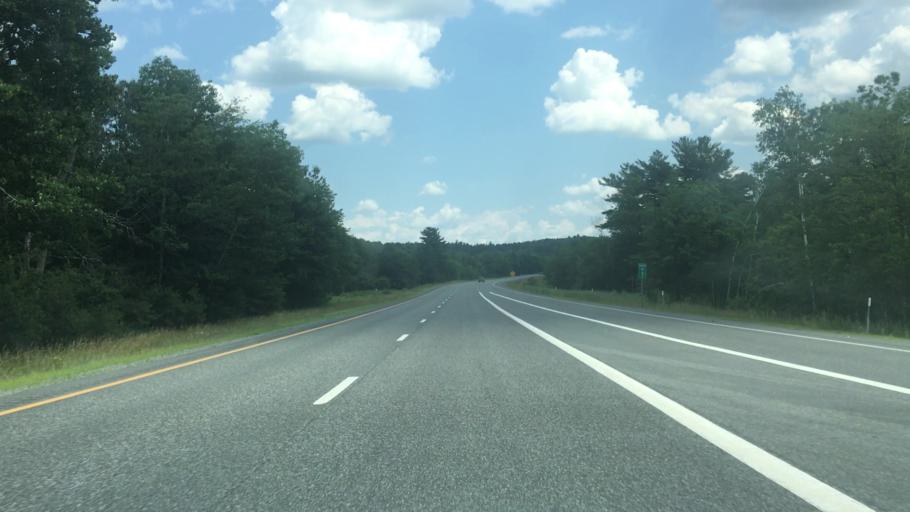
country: US
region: New Hampshire
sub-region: Sullivan County
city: Sunapee
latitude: 43.4408
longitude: -72.0609
